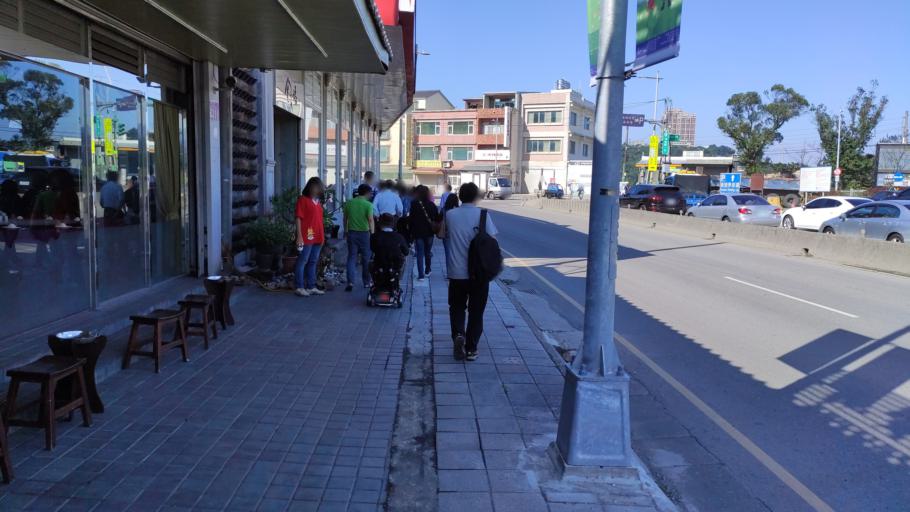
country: TW
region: Taiwan
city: Daxi
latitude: 24.8850
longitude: 121.2802
